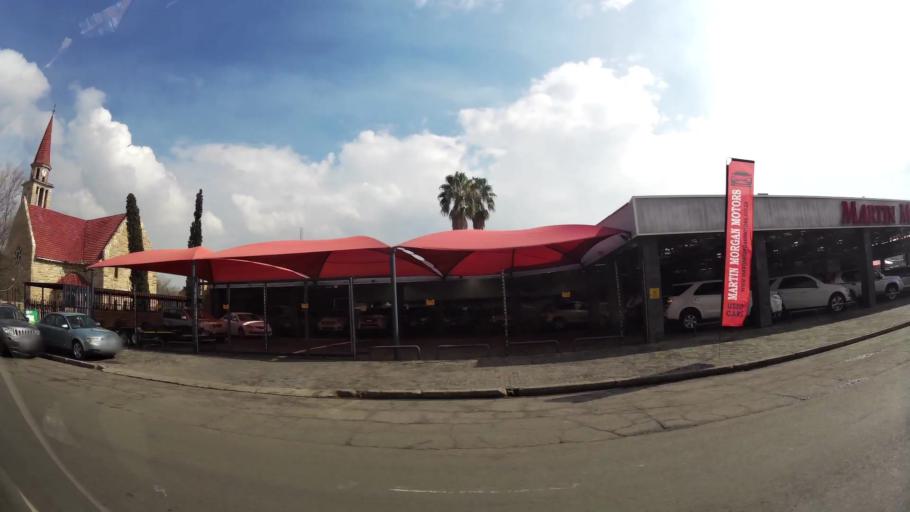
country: ZA
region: Gauteng
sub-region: Sedibeng District Municipality
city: Vereeniging
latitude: -26.6698
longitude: 27.9304
